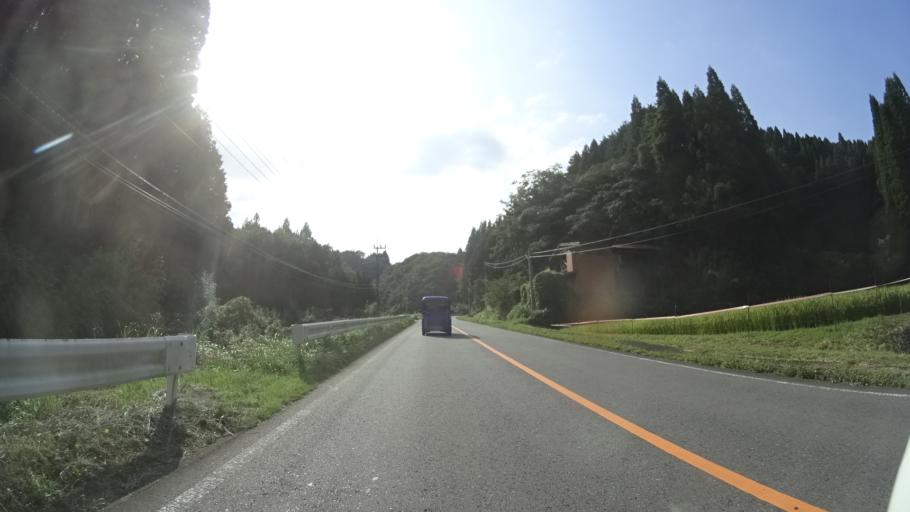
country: JP
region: Kumamoto
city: Ozu
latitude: 32.6775
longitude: 131.0294
